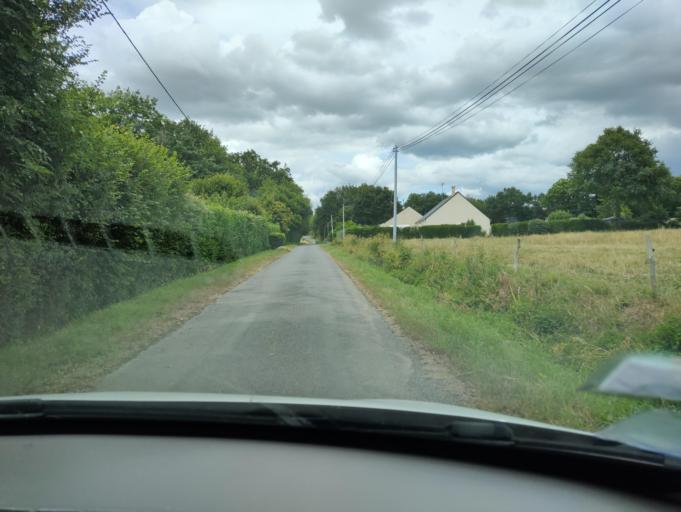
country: FR
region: Pays de la Loire
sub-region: Departement de la Loire-Atlantique
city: Chateaubriant
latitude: 47.7034
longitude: -1.4258
